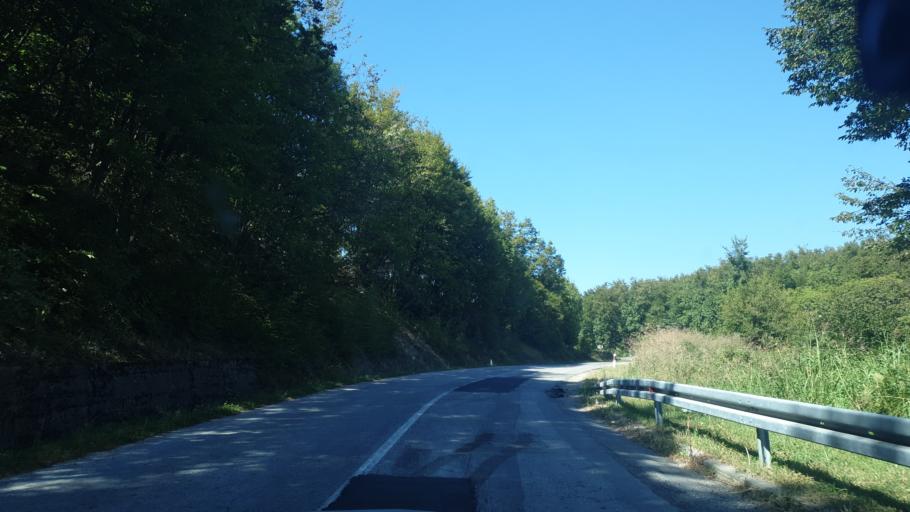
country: RS
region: Central Serbia
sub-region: Kolubarski Okrug
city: Mionica
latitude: 44.1509
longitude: 20.0205
